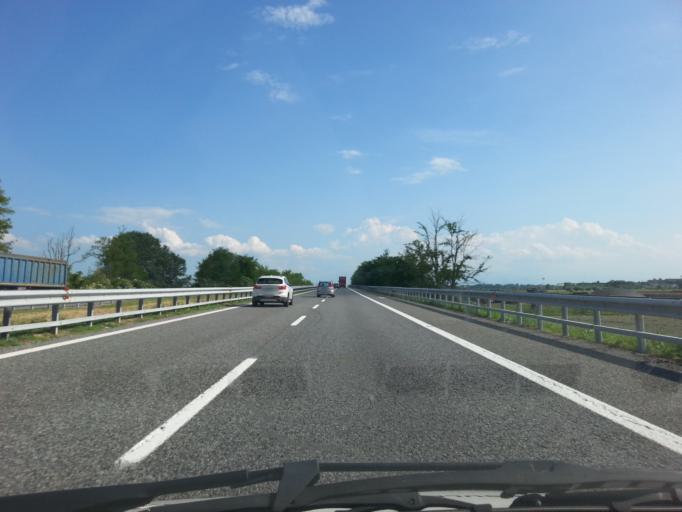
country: IT
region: Piedmont
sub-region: Provincia di Cuneo
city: Marene
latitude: 44.6993
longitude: 7.7644
